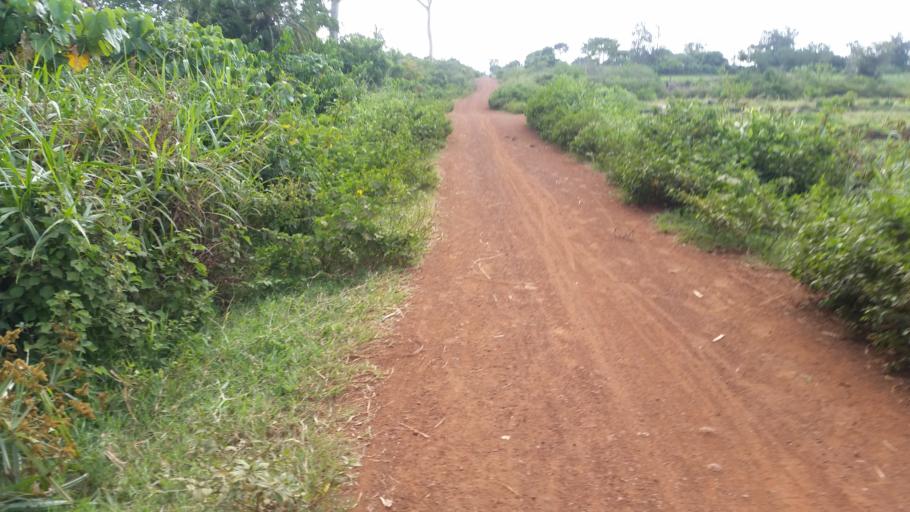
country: UG
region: Eastern Region
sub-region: Busia District
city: Busia
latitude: 0.5492
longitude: 34.0102
